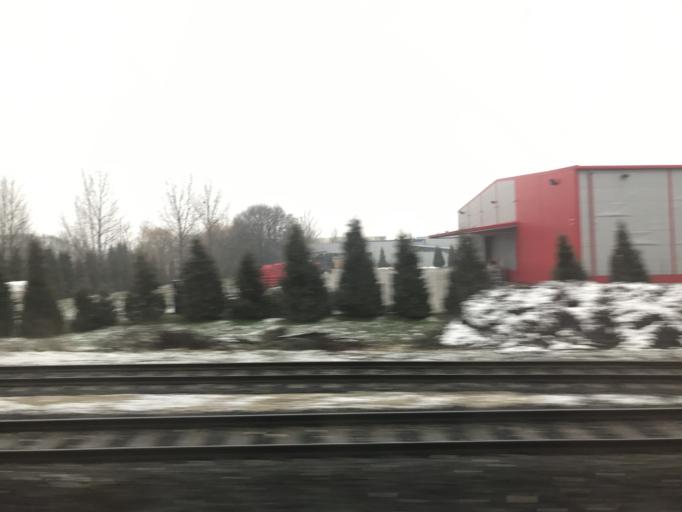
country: HU
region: Gyor-Moson-Sopron
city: Gyor
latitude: 47.6838
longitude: 17.6899
